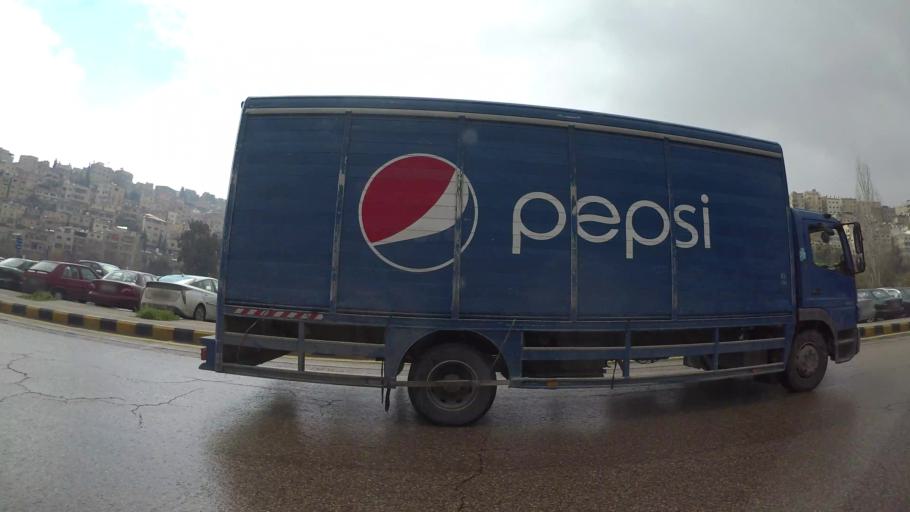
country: JO
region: Amman
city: Amman
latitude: 31.9452
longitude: 35.9218
